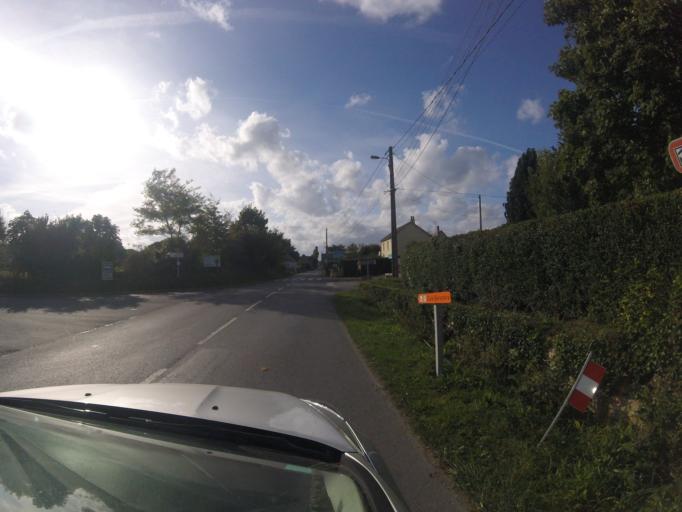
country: FR
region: Lower Normandy
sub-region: Departement du Calvados
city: Port-en-Bessin-Huppain
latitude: 49.3492
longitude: -0.8201
